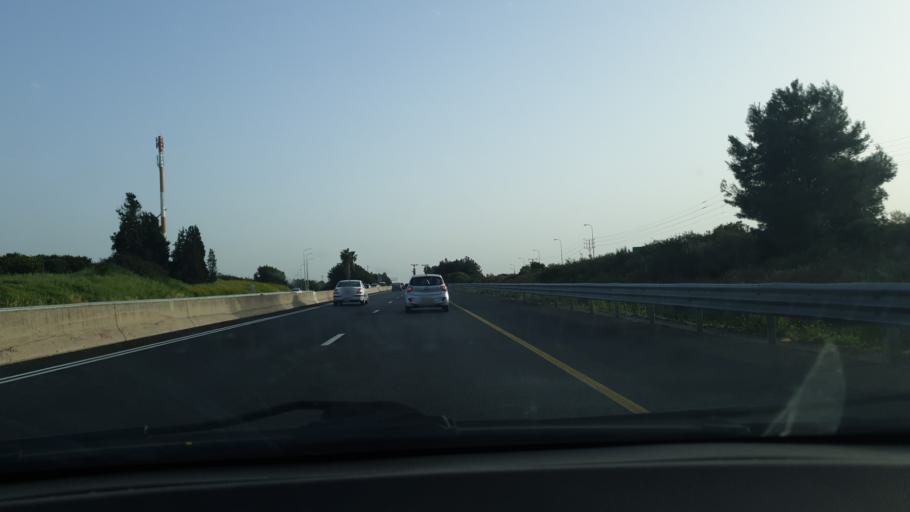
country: IL
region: Central District
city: Even Yehuda
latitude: 32.2387
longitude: 34.8863
